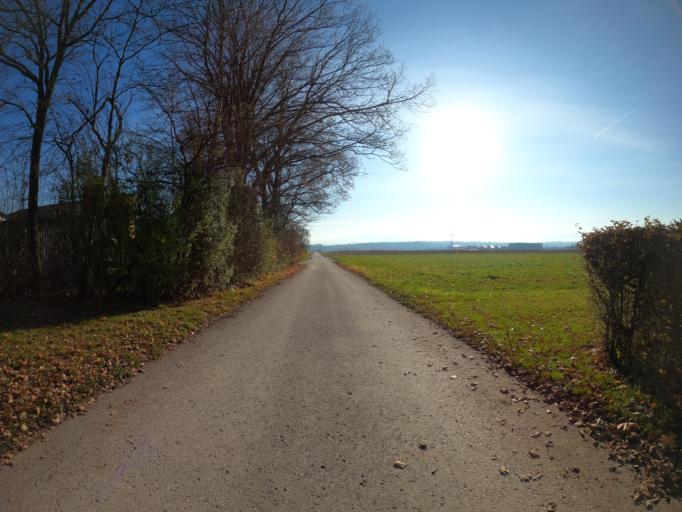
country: DE
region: Baden-Wuerttemberg
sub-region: Regierungsbezirk Stuttgart
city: Schlierbach
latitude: 48.6845
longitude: 9.5344
